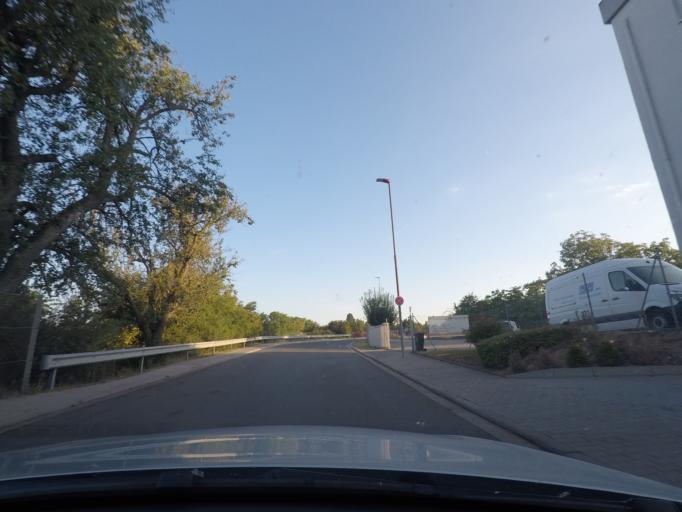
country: DE
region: Rheinland-Pfalz
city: Kirchheimbolanden
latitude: 49.6725
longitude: 8.0134
